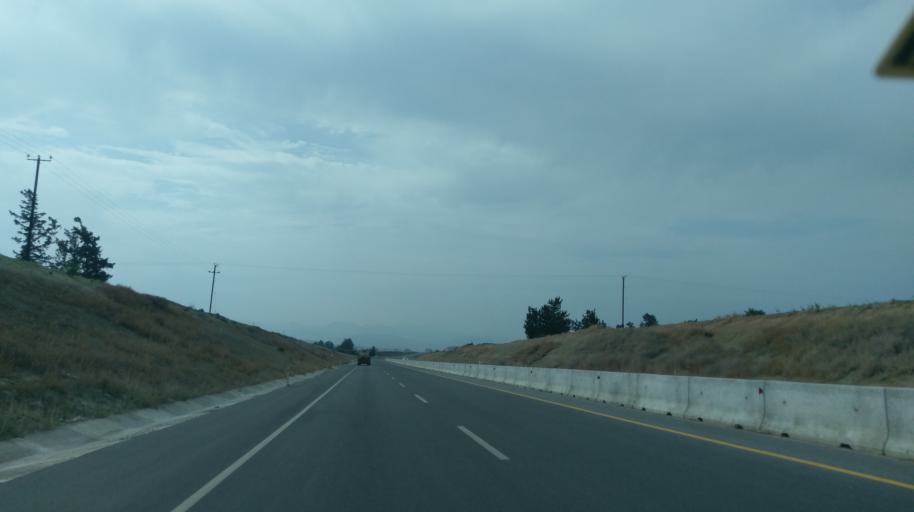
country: CY
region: Lefkosia
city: Morfou
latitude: 35.1637
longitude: 32.9323
